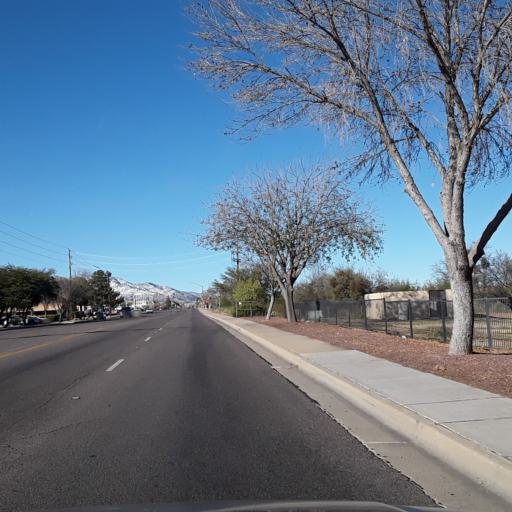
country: US
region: Arizona
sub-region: Cochise County
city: Sierra Vista
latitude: 31.5547
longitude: -110.2693
